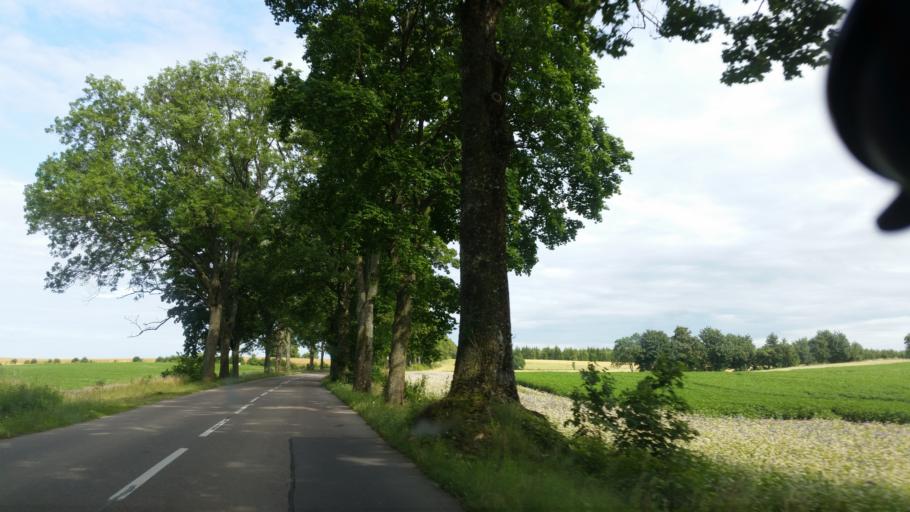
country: PL
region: Pomeranian Voivodeship
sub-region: Powiat wejherowski
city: Choczewo
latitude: 54.7245
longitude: 17.8718
